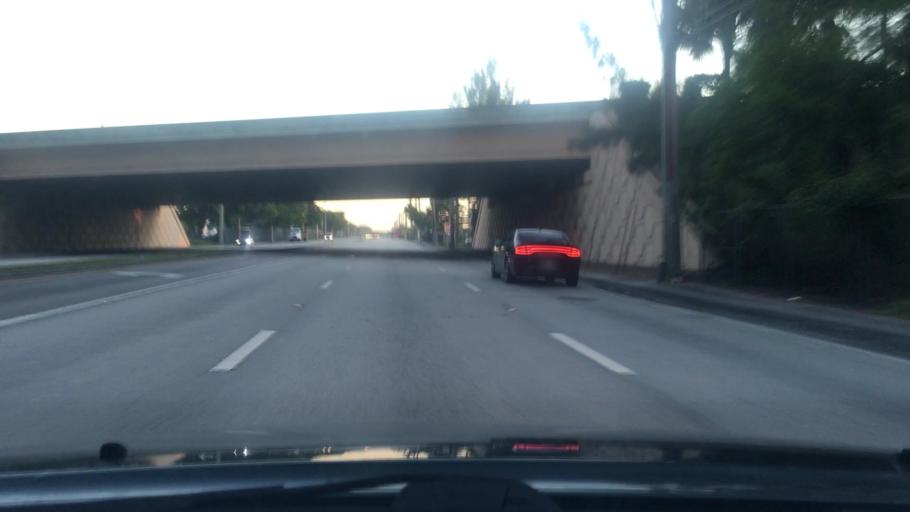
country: US
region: Florida
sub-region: Miami-Dade County
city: Opa-locka
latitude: 25.8839
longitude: -80.2683
